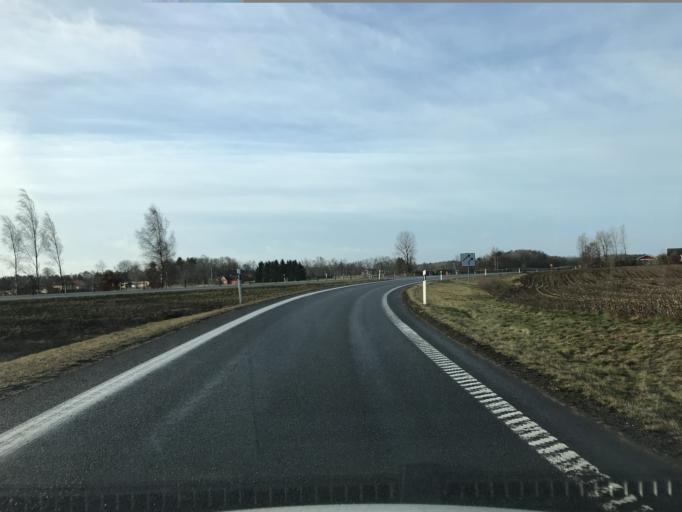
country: SE
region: Skane
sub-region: Hassleholms Kommun
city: Hassleholm
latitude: 56.1813
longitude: 13.7517
